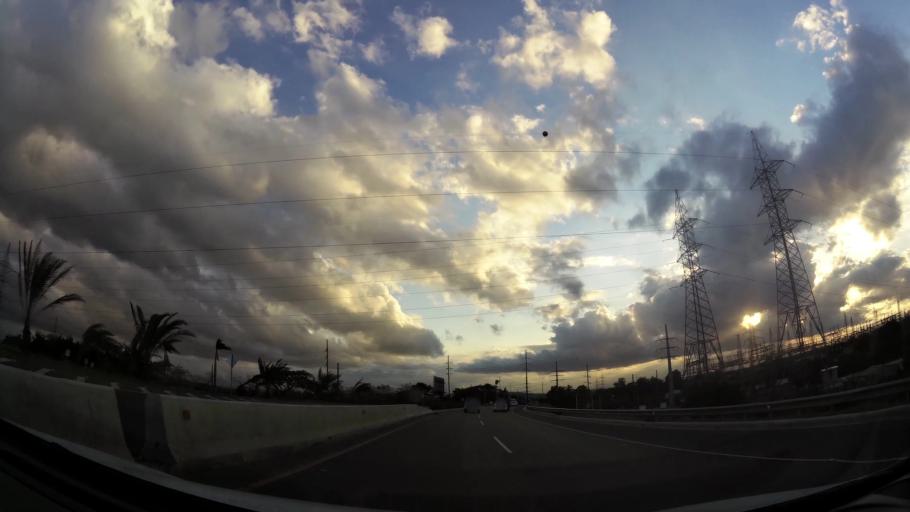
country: DO
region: Santiago
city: Licey al Medio
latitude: 19.4155
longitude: -70.6421
